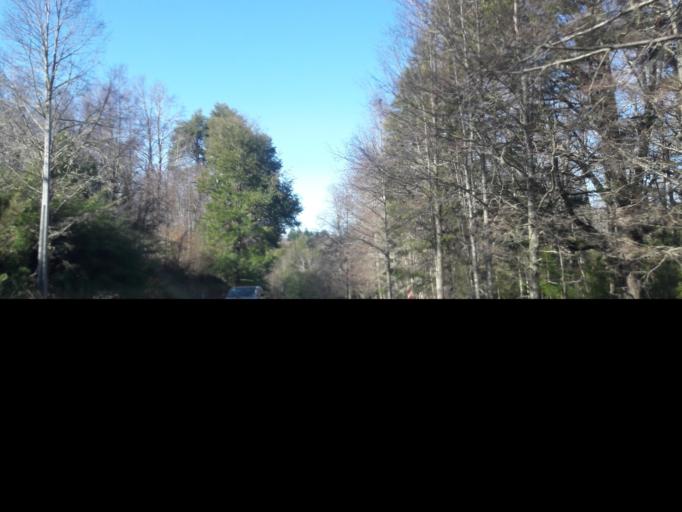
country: CL
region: Araucania
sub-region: Provincia de Malleco
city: Victoria
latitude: -38.3316
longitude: -71.9764
